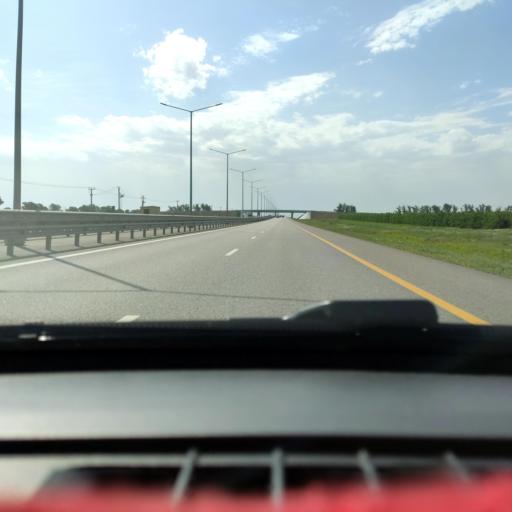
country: RU
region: Voronezj
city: Podkletnoye
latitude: 51.5739
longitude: 39.4687
